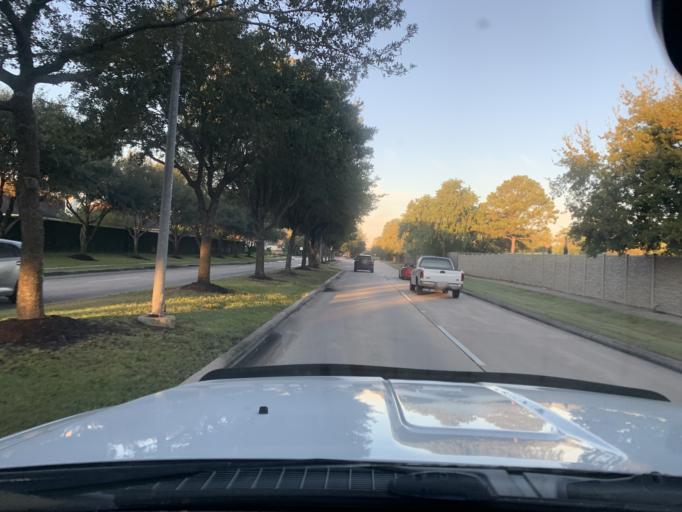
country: US
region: Texas
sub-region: Fort Bend County
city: Sugar Land
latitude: 29.6512
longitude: -95.6268
